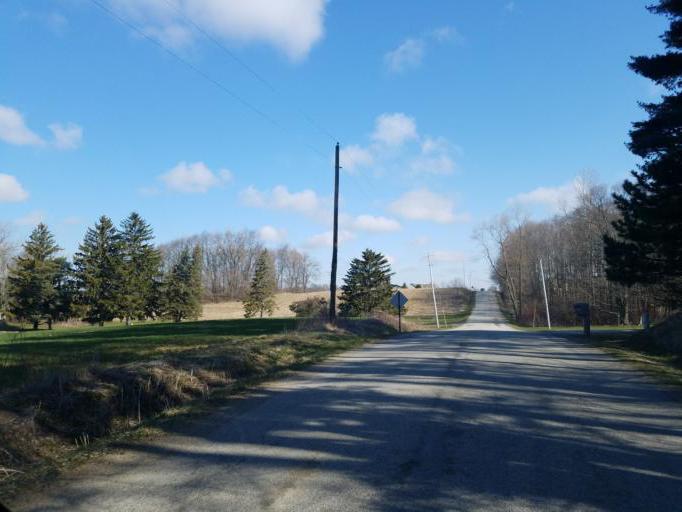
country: US
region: Ohio
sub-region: Morrow County
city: Mount Gilead
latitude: 40.5946
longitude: -82.7477
